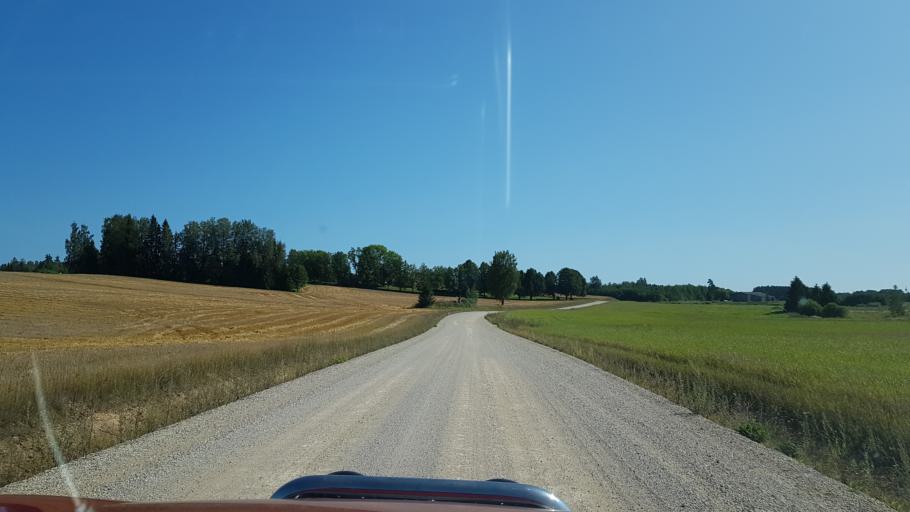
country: EE
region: Vorumaa
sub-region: Voru linn
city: Voru
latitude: 57.7361
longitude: 27.2443
